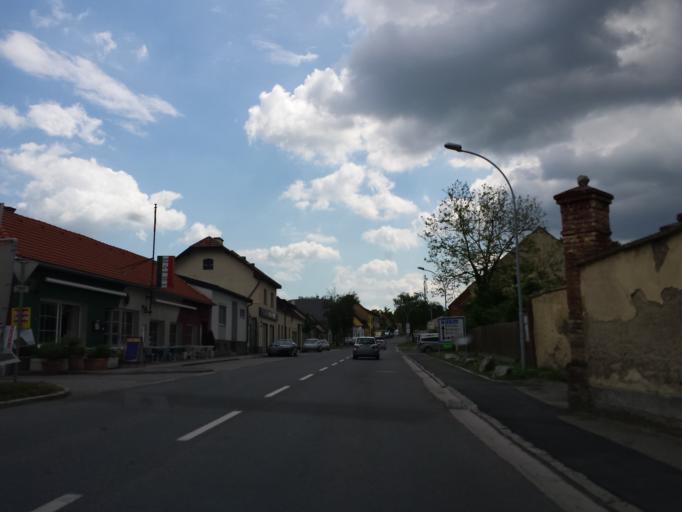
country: AT
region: Lower Austria
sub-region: Politischer Bezirk Wien-Umgebung
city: Fischamend Dorf
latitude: 48.1193
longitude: 16.6149
